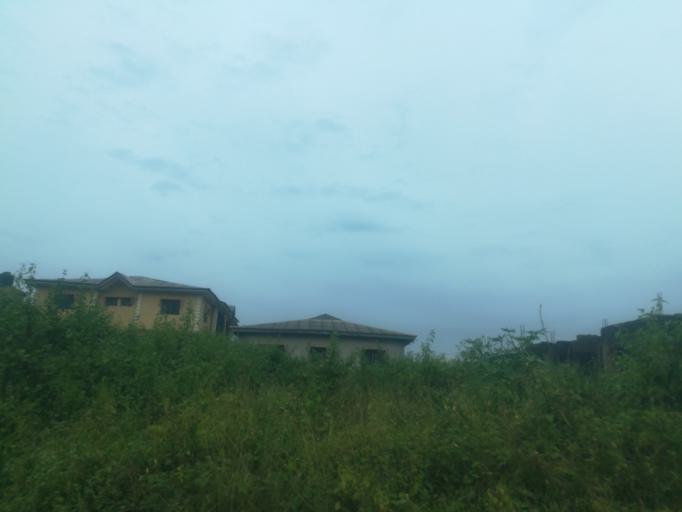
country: NG
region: Oyo
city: Egbeda
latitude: 7.3850
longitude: 3.9958
